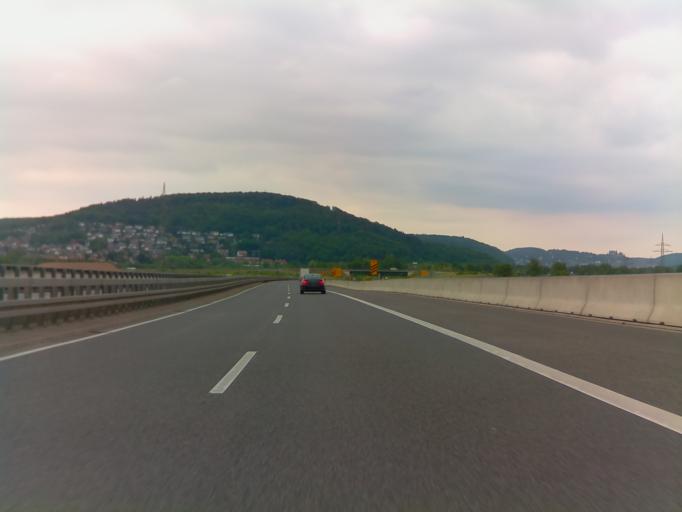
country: DE
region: Hesse
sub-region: Regierungsbezirk Giessen
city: Fronhausen
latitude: 50.7461
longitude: 8.7402
